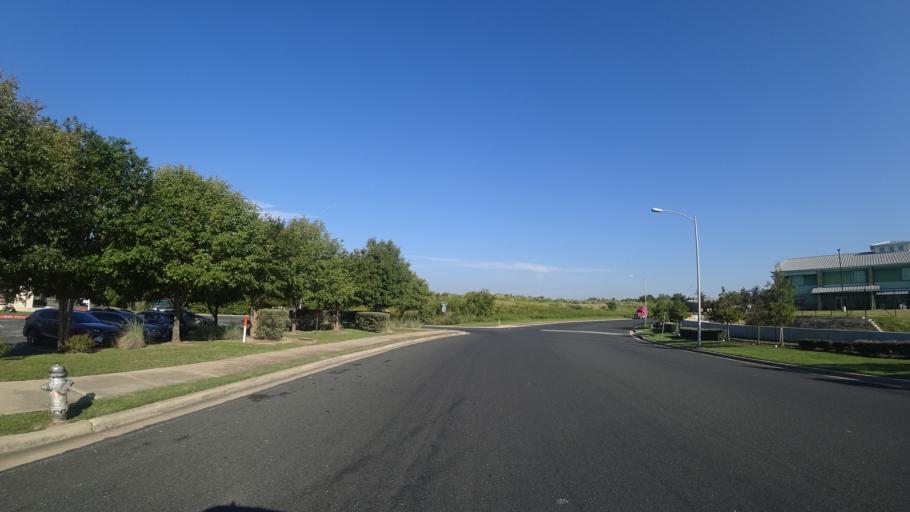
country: US
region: Texas
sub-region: Travis County
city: Austin
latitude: 30.3314
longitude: -97.6737
